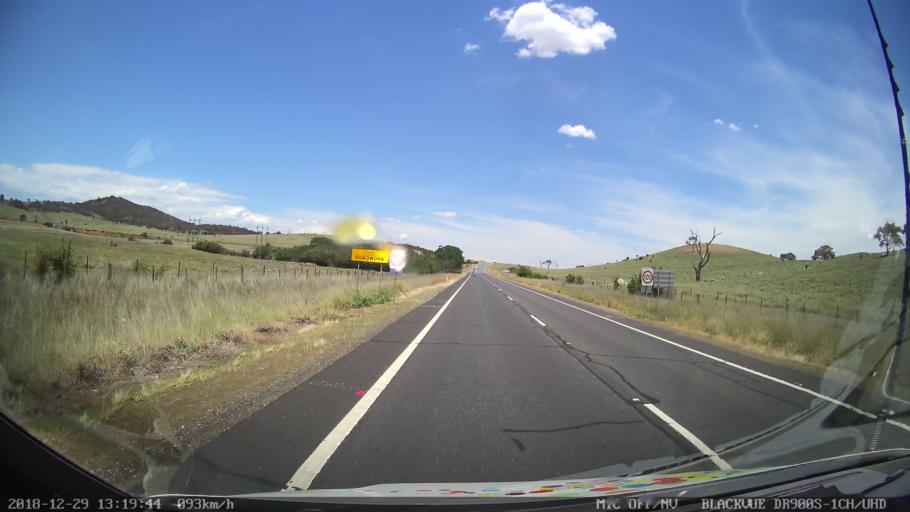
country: AU
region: Australian Capital Territory
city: Macarthur
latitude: -35.7696
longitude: 149.1615
